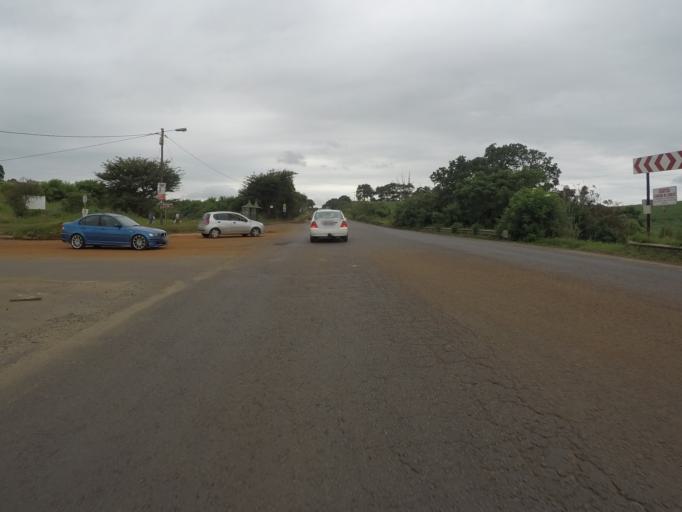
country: ZA
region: KwaZulu-Natal
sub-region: uThungulu District Municipality
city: Empangeni
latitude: -28.7778
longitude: 31.8819
